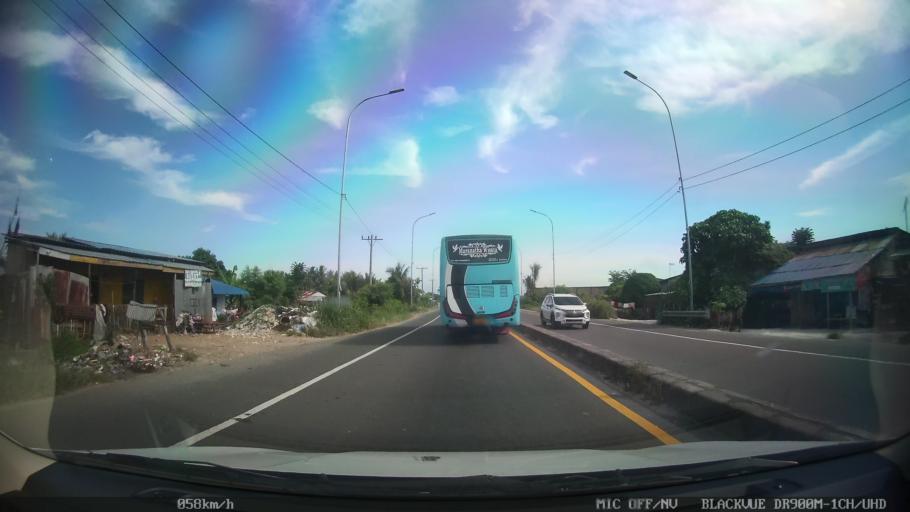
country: ID
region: North Sumatra
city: Sunggal
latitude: 3.6182
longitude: 98.6289
